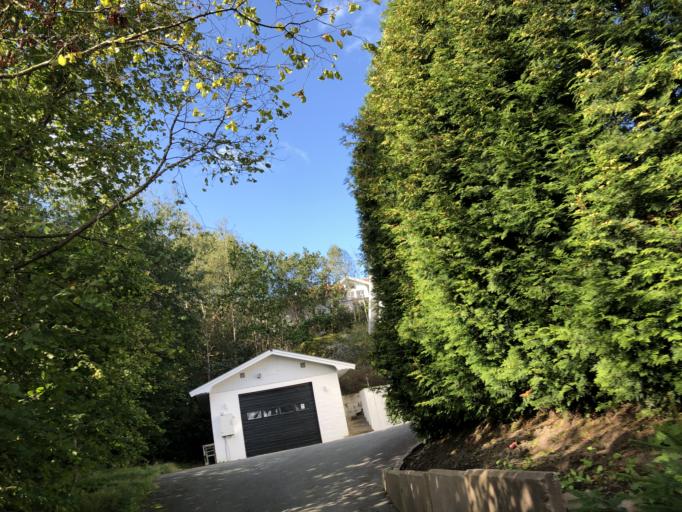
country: SE
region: Vaestra Goetaland
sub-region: Goteborg
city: Torslanda
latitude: 57.7465
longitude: 11.8262
